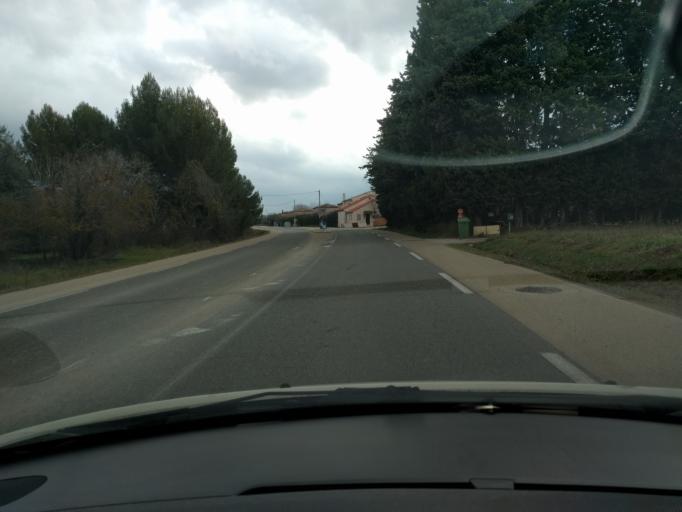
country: FR
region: Provence-Alpes-Cote d'Azur
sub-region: Departement des Bouches-du-Rhone
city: Bouc-Bel-Air
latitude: 43.4347
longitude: 5.4079
